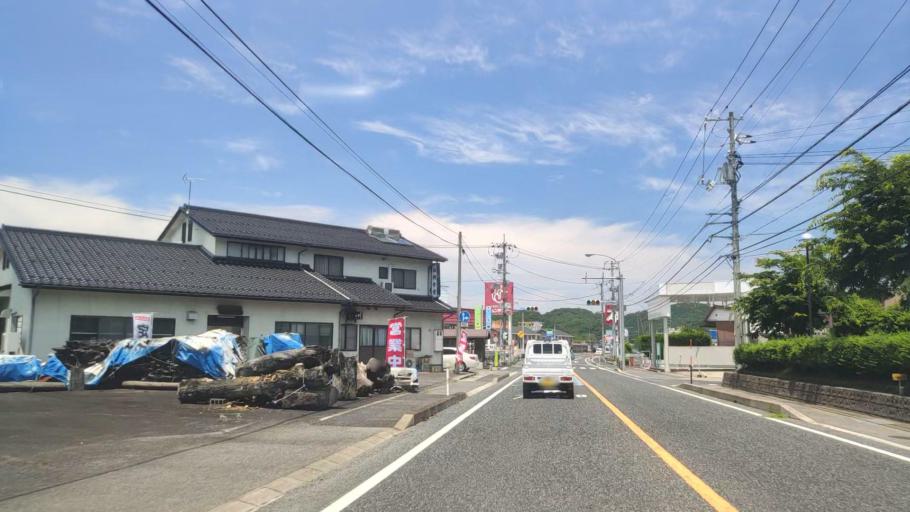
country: JP
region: Tottori
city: Tottori
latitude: 35.4153
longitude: 134.2557
